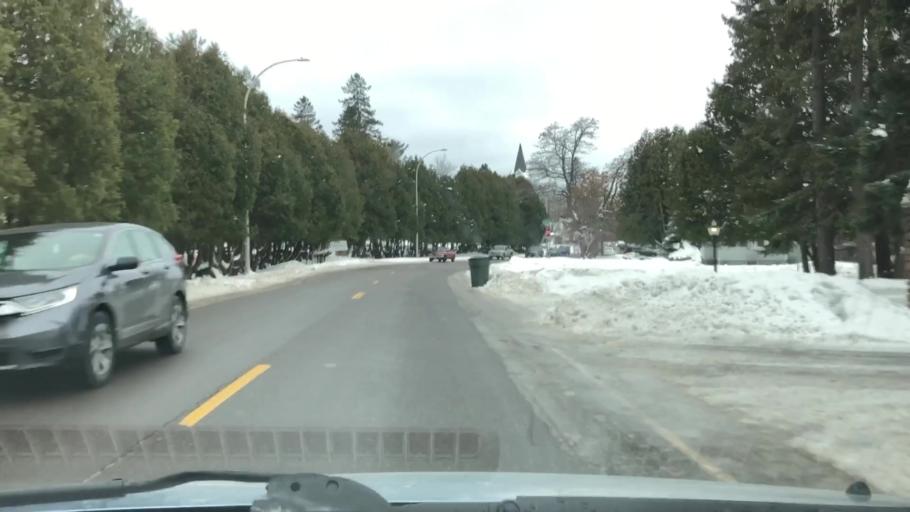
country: US
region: Minnesota
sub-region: Carlton County
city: Carlton
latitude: 46.6642
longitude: -92.4177
